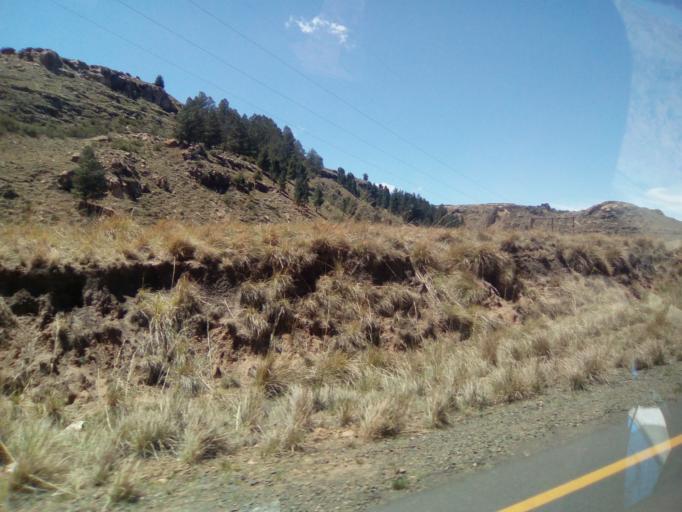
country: LS
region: Qacha's Nek
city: Qacha's Nek
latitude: -30.1042
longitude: 28.6565
